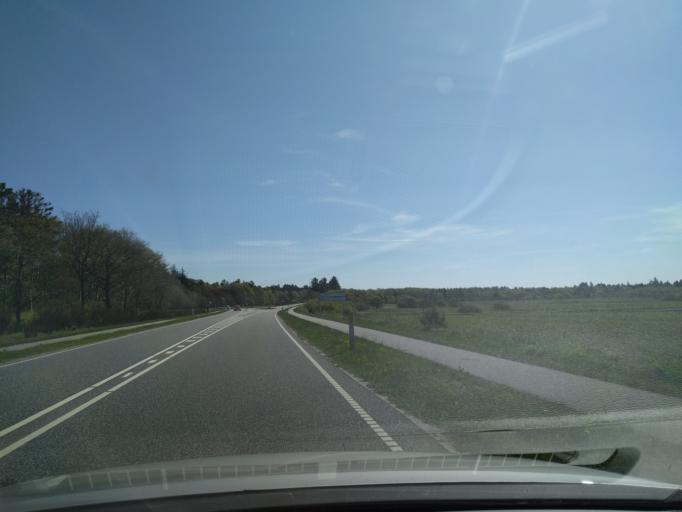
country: DK
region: Central Jutland
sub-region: Ringkobing-Skjern Kommune
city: Ringkobing
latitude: 56.0866
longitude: 8.2963
